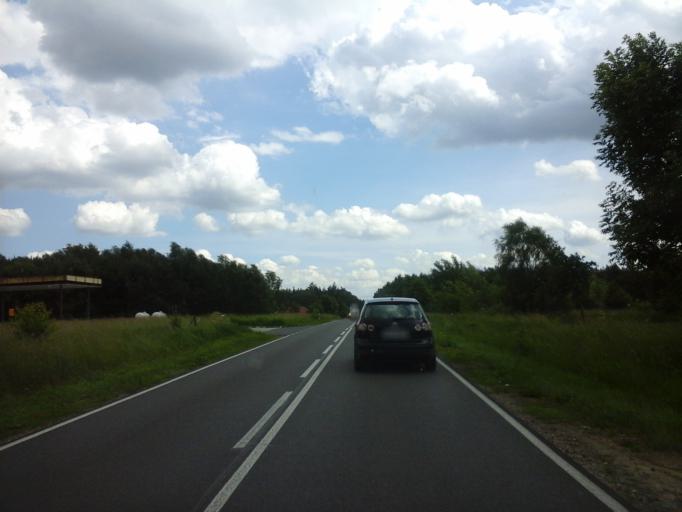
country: PL
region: West Pomeranian Voivodeship
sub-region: Powiat swidwinski
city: Slawoborze
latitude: 53.8829
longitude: 15.7217
